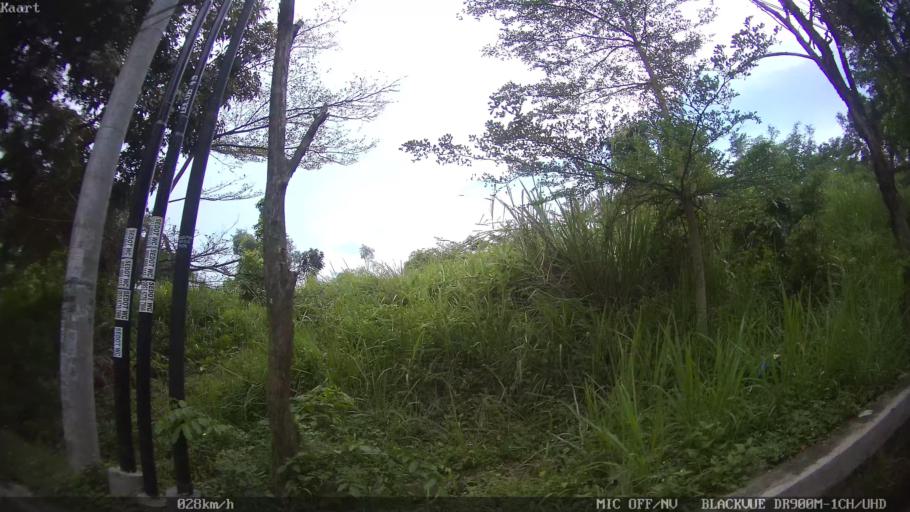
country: ID
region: Lampung
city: Kedaton
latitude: -5.3810
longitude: 105.2115
